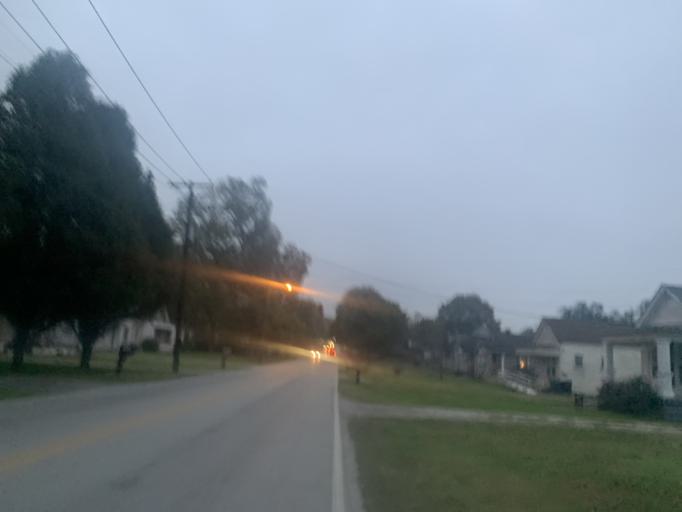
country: US
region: Kentucky
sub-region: Jefferson County
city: Shively
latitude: 38.2150
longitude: -85.8001
